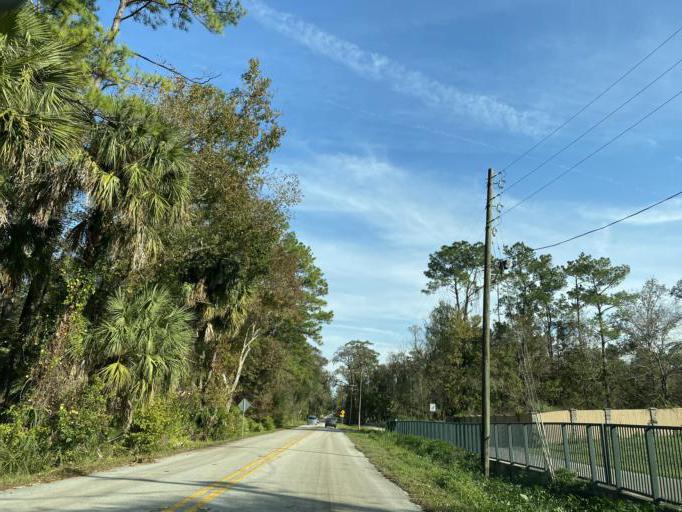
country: US
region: Florida
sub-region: Seminole County
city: Longwood
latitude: 28.7216
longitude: -81.3338
